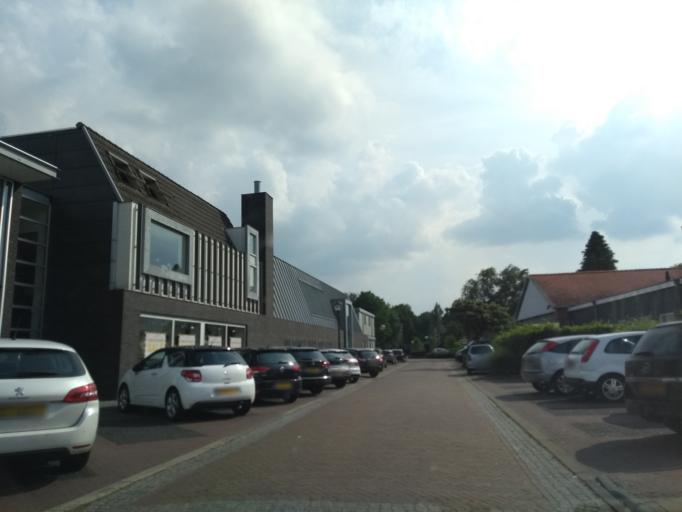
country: NL
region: Overijssel
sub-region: Gemeente Staphorst
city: Staphorst
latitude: 52.6728
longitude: 6.2849
